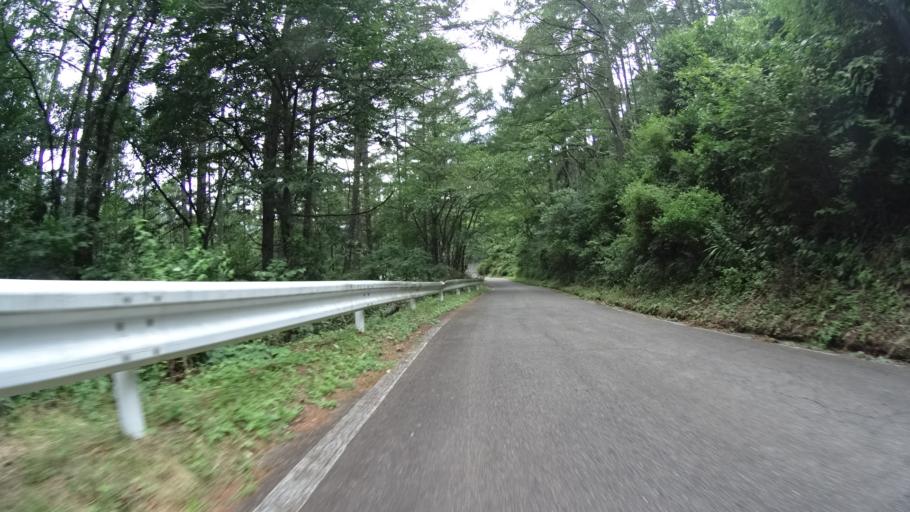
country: JP
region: Nagano
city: Saku
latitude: 36.0702
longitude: 138.6337
